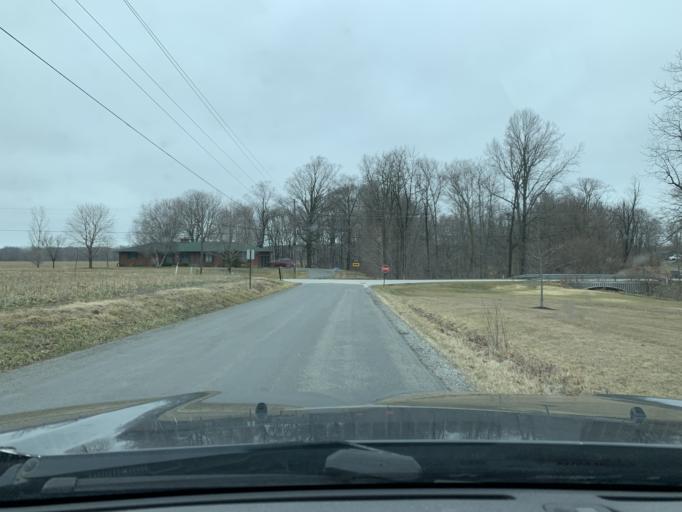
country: US
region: Indiana
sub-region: Porter County
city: Chesterton
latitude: 41.6063
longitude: -86.9900
